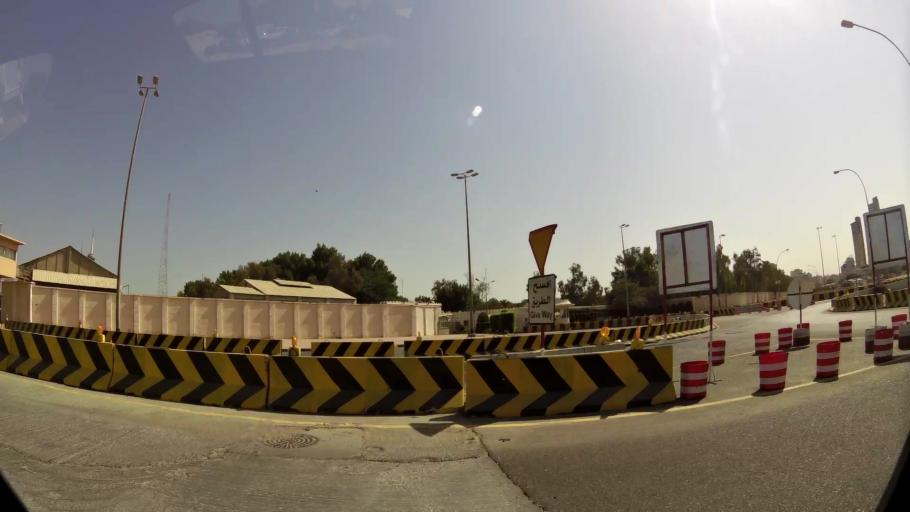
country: KW
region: Al Asimah
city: Ad Dasmah
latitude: 29.3869
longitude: 47.9950
